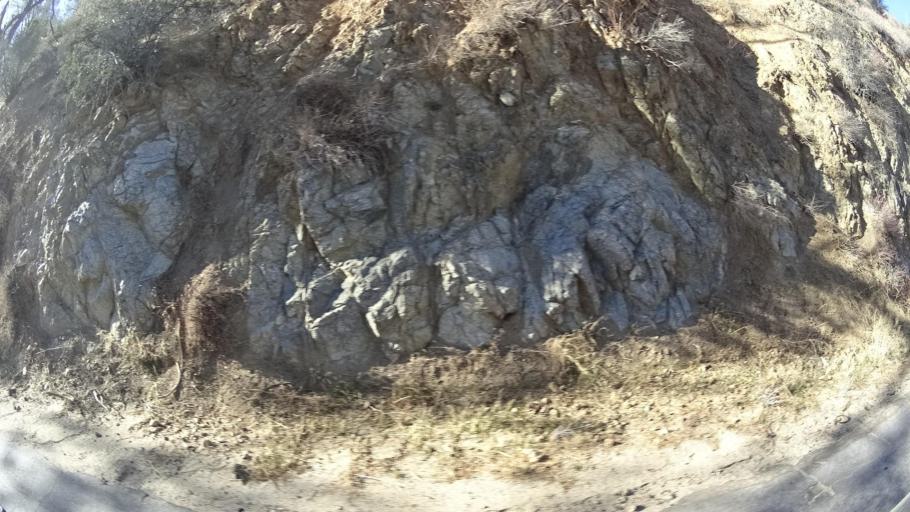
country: US
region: California
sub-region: Kern County
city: Bodfish
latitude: 35.5701
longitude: -118.5070
